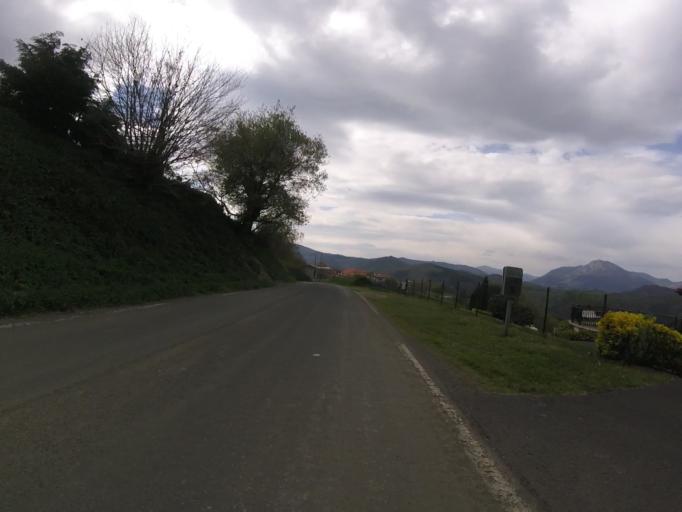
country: ES
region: Basque Country
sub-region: Provincia de Guipuzcoa
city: Aizarnazabal
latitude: 43.2509
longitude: -2.1963
